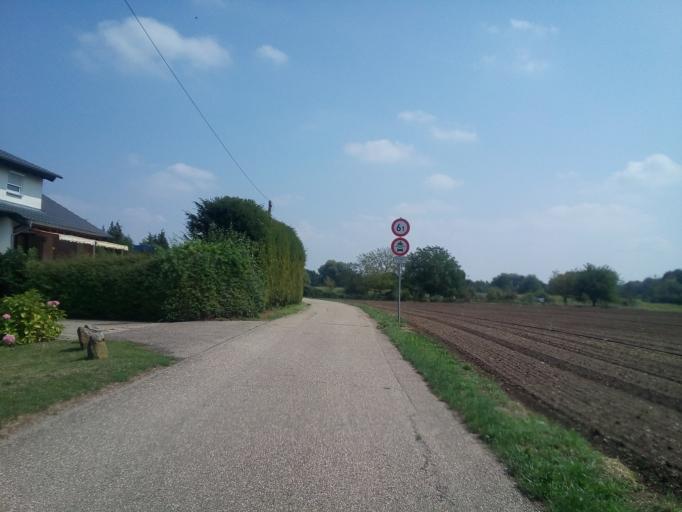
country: DE
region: Baden-Wuerttemberg
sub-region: Freiburg Region
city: Kehl
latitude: 48.6026
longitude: 7.8467
